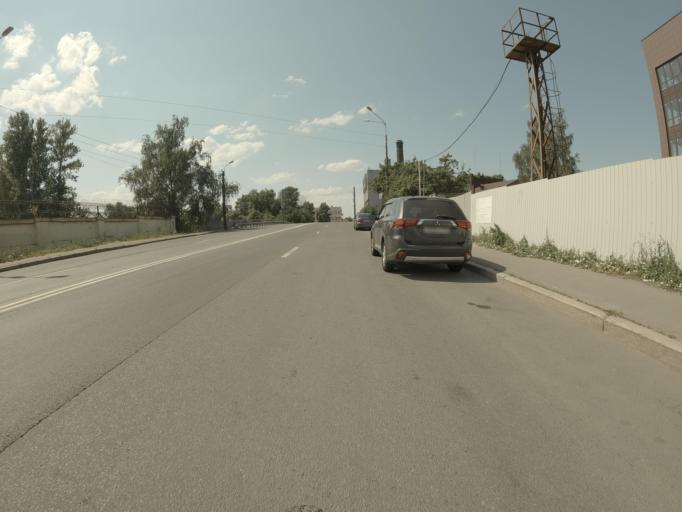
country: RU
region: St.-Petersburg
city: Admiralteisky
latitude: 59.9129
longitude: 30.2631
